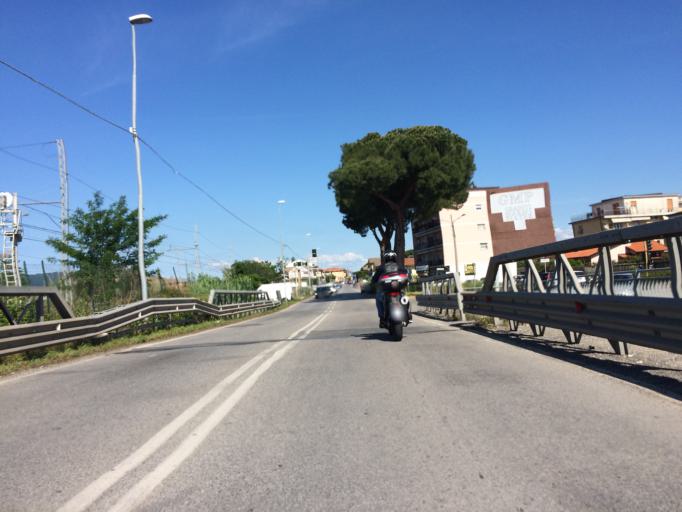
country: IT
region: Liguria
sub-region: Provincia di La Spezia
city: Casano-Dogana-Isola
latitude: 44.0636
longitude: 10.0359
